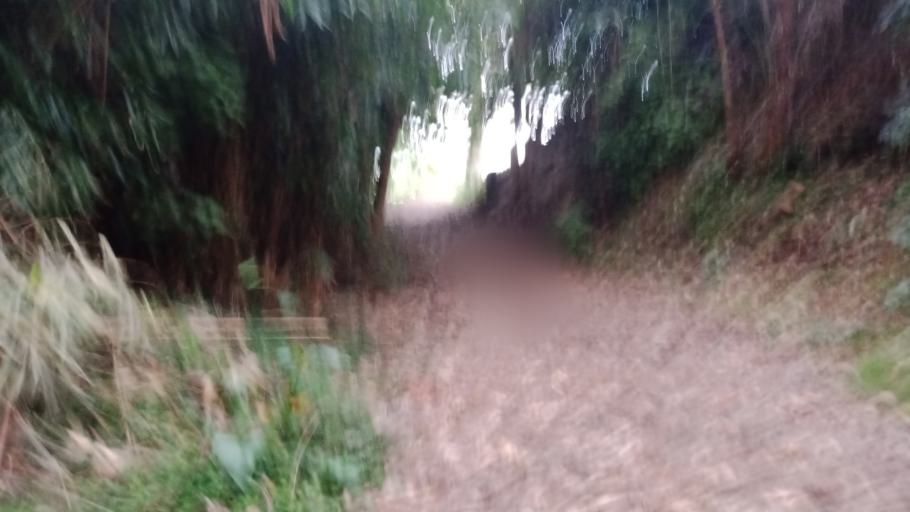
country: NZ
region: Gisborne
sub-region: Gisborne District
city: Gisborne
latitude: -38.6398
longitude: 178.0177
